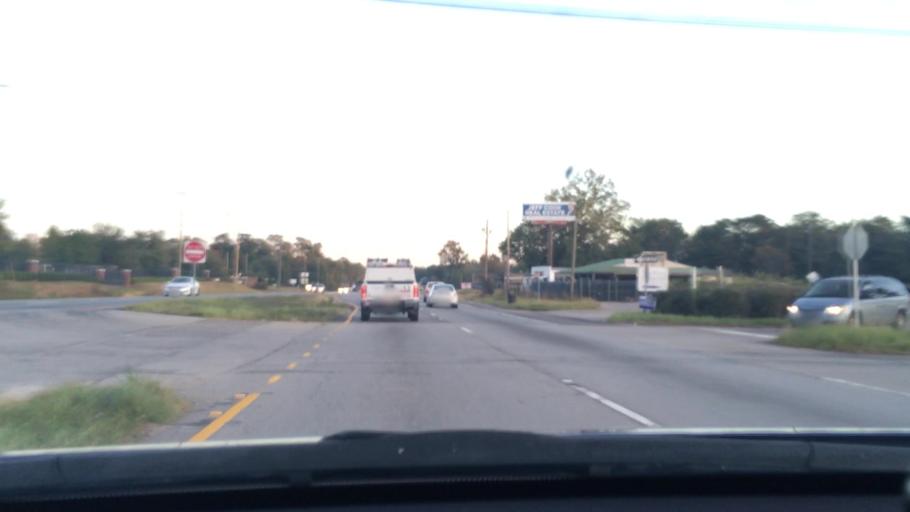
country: US
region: South Carolina
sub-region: Richland County
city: Hopkins
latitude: 33.9508
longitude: -80.9173
